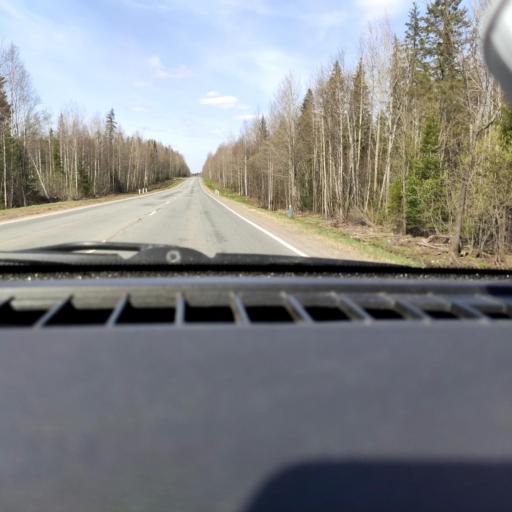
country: RU
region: Perm
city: Polazna
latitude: 58.2759
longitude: 56.1660
